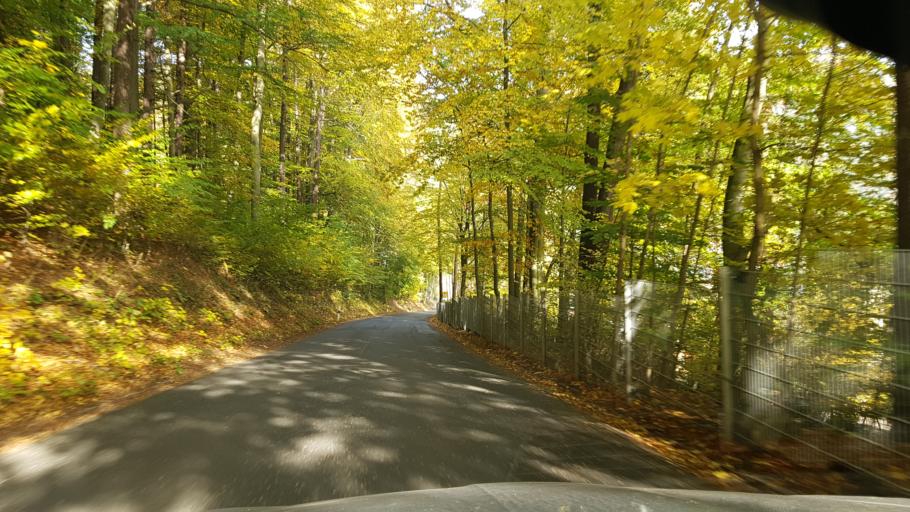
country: DE
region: Saxony
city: Konigstein
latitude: 50.9109
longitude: 14.0523
